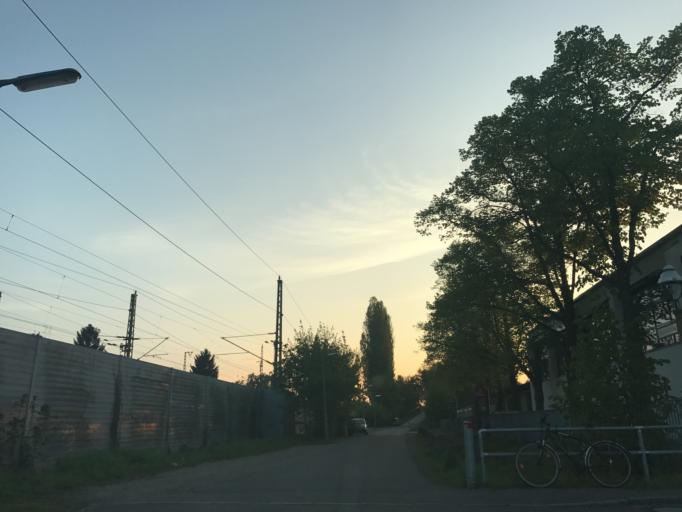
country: DE
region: Berlin
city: Staaken
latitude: 52.5377
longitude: 13.1464
